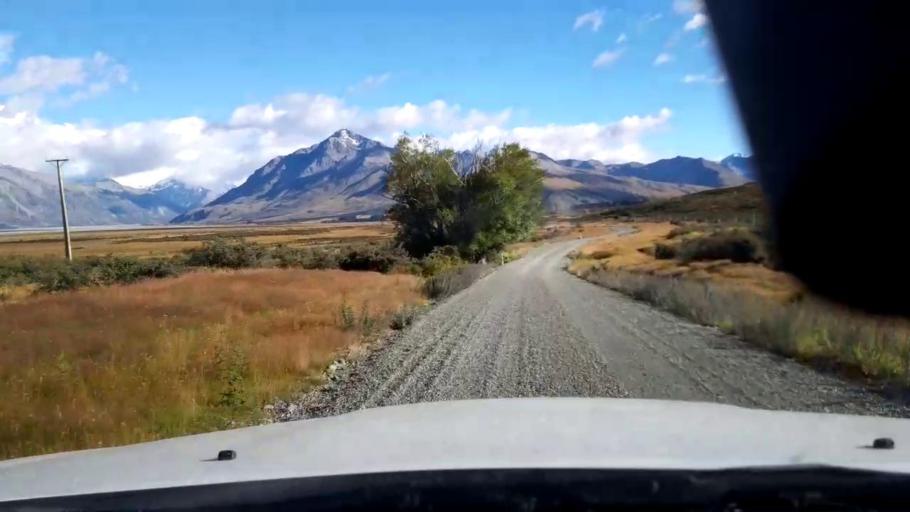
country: NZ
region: Canterbury
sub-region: Timaru District
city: Pleasant Point
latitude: -43.7503
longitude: 170.5711
